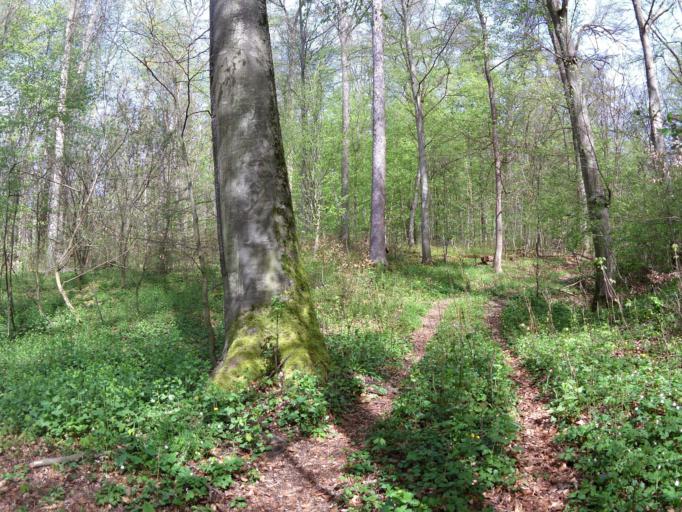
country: DE
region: Bavaria
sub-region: Regierungsbezirk Unterfranken
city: Rimpar
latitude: 49.8635
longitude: 9.9897
